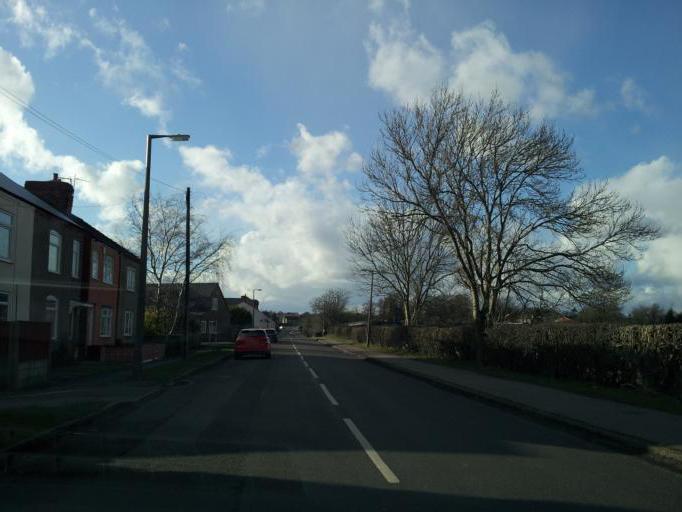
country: GB
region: England
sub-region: Derbyshire
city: Shirland
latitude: 53.1195
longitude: -1.3992
